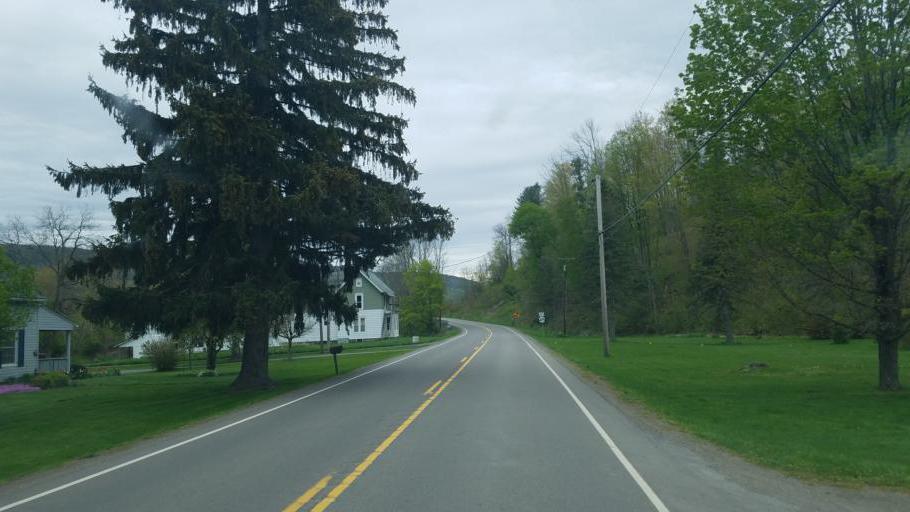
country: US
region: Pennsylvania
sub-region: Tioga County
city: Westfield
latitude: 41.9606
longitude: -77.4454
